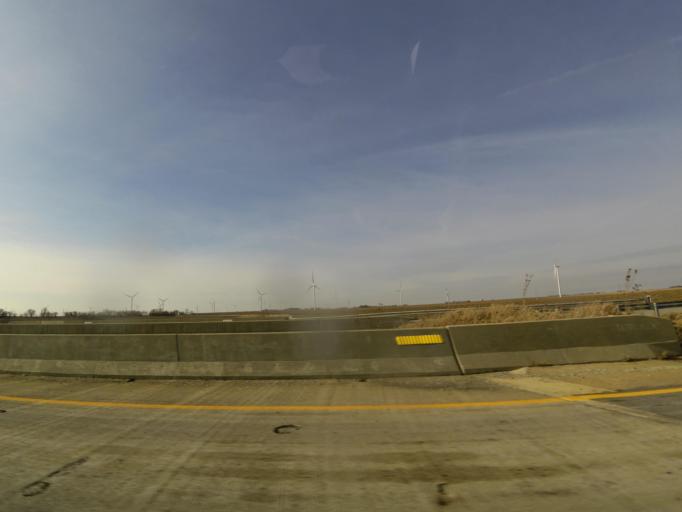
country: US
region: Illinois
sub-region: Macon County
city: Maroa
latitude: 40.0451
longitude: -88.9656
